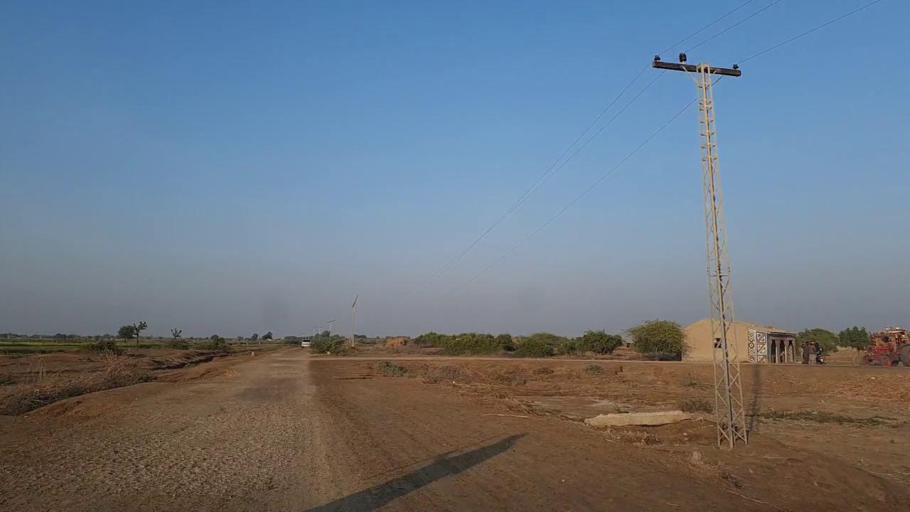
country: PK
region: Sindh
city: Naukot
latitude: 24.9480
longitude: 69.4464
